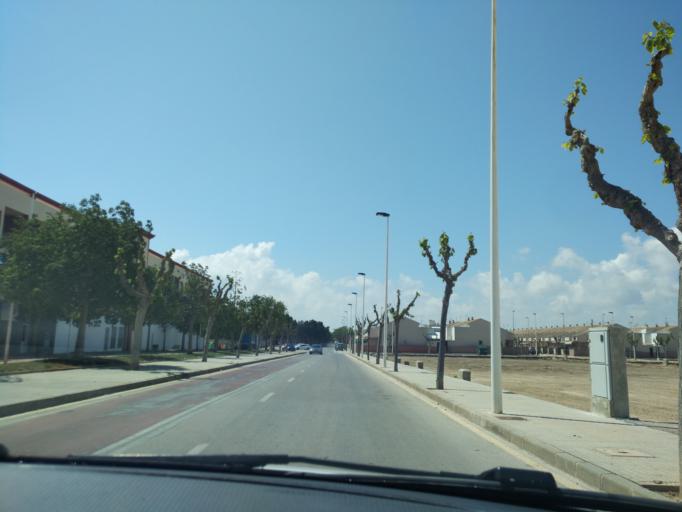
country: ES
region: Murcia
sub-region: Murcia
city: Los Alcazares
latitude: 37.7504
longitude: -0.8481
